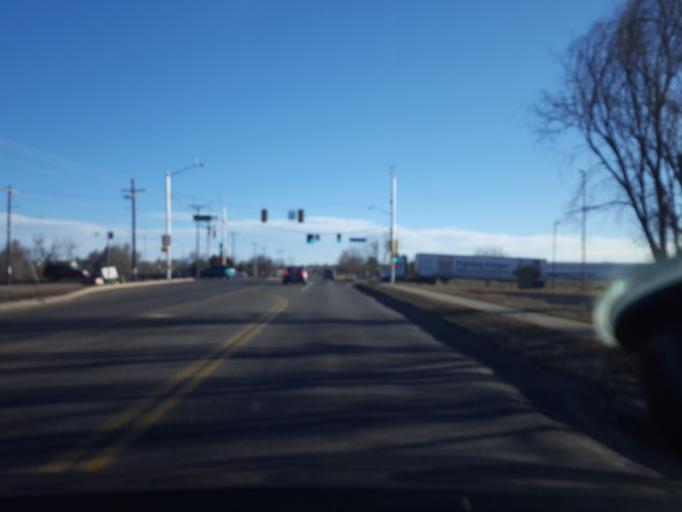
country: US
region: Colorado
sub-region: Adams County
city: Aurora
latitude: 39.7464
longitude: -104.7725
